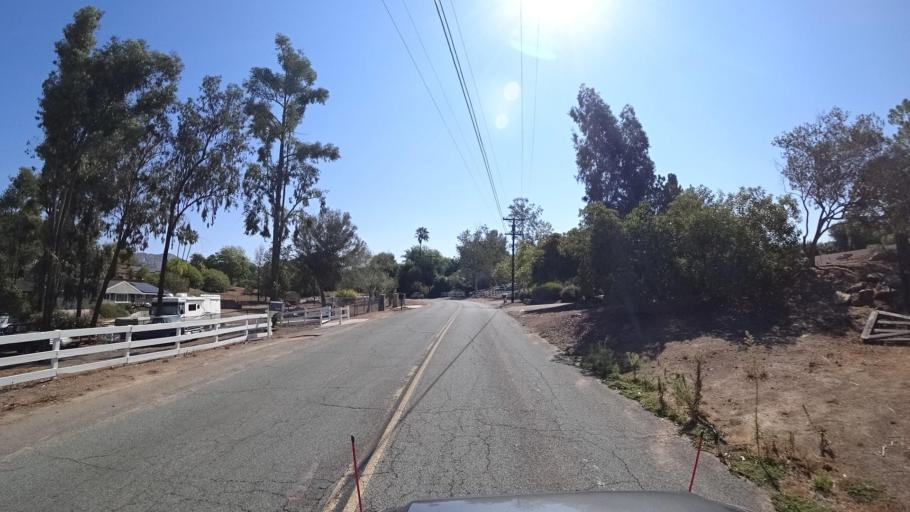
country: US
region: California
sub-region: San Diego County
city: Granite Hills
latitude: 32.7895
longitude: -116.9107
